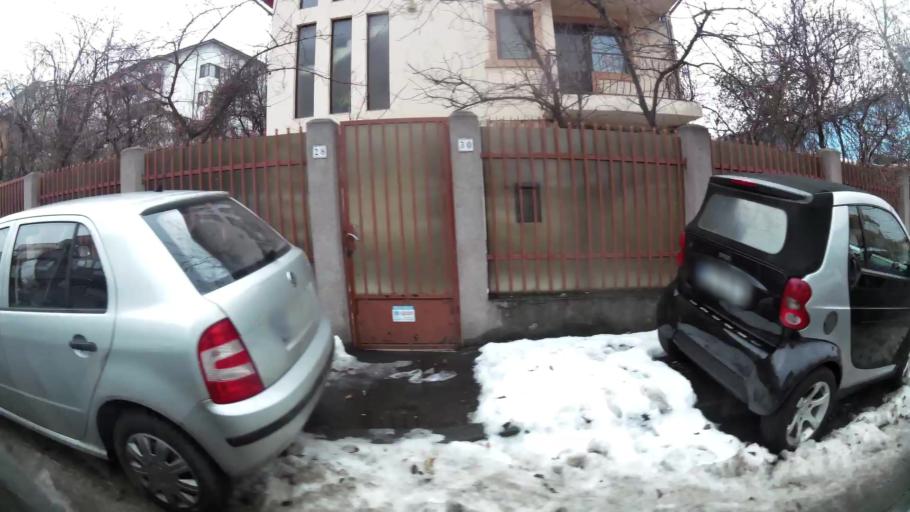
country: RO
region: Bucuresti
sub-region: Municipiul Bucuresti
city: Bucharest
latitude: 44.4083
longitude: 26.1307
